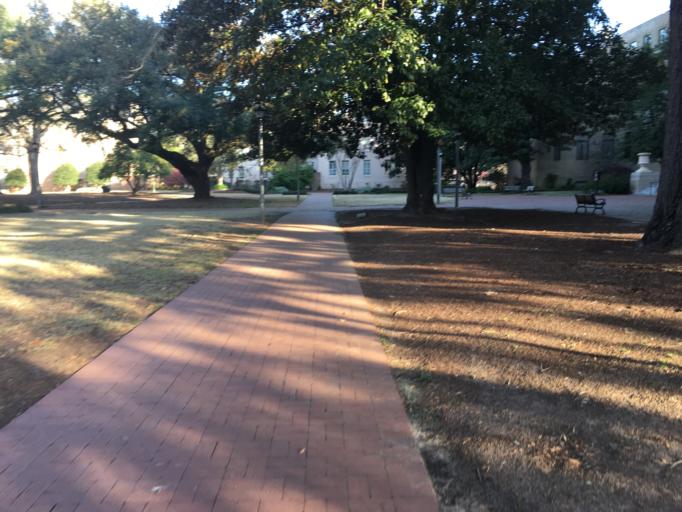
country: US
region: South Carolina
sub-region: Richland County
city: Columbia
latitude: 33.9984
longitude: -81.0271
